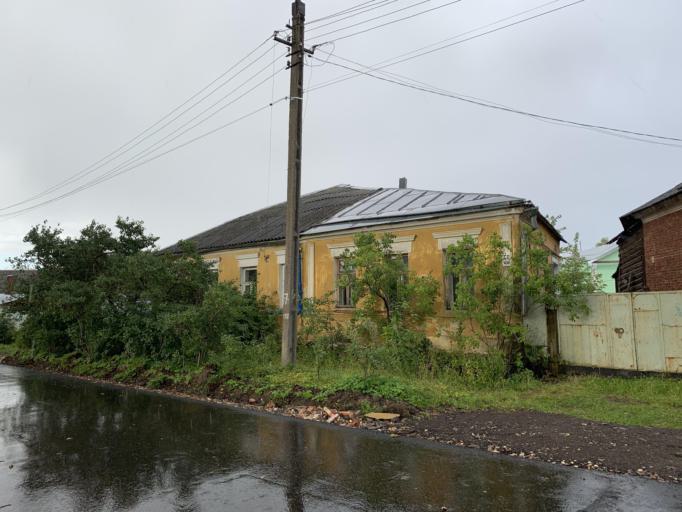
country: RU
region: Tverskaya
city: Vyshniy Volochek
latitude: 57.5856
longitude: 34.5527
